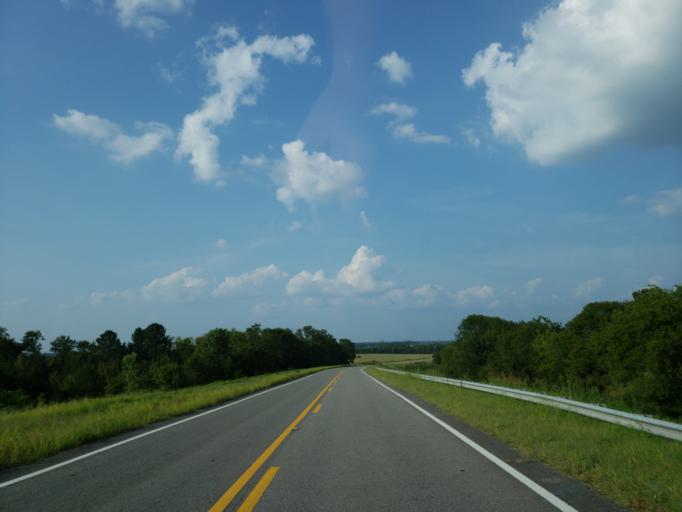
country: US
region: Alabama
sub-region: Greene County
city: Eutaw
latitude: 32.7879
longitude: -87.9753
